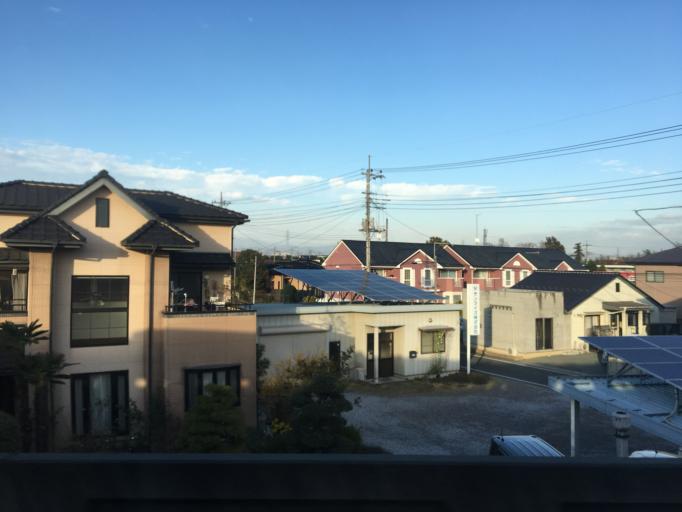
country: JP
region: Gunma
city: Isesaki
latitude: 36.3302
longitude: 139.1851
